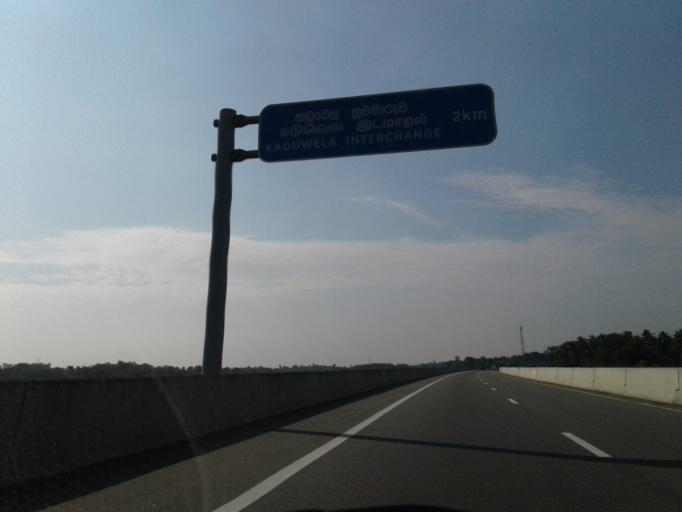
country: LK
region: Western
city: Mulleriyawa
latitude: 6.9595
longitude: 79.9761
